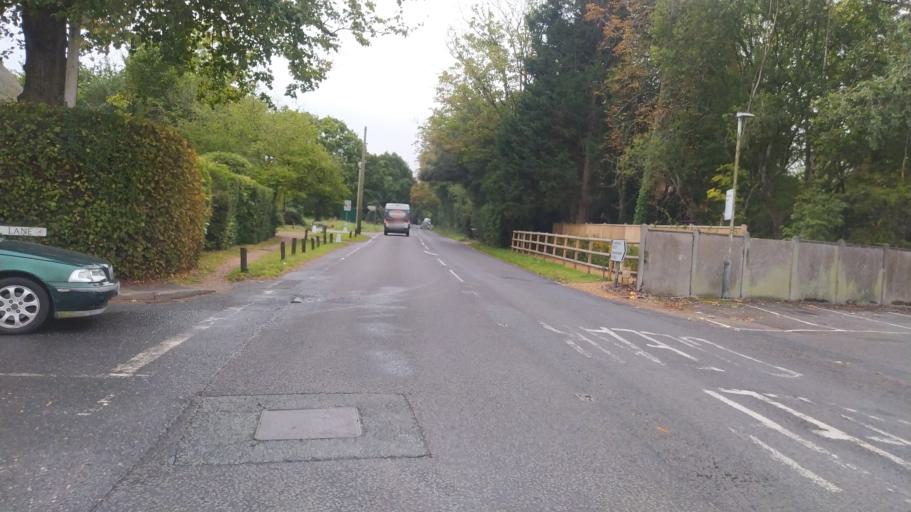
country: GB
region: England
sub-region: Hampshire
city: Brockenhurst
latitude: 50.8173
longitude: -1.5720
